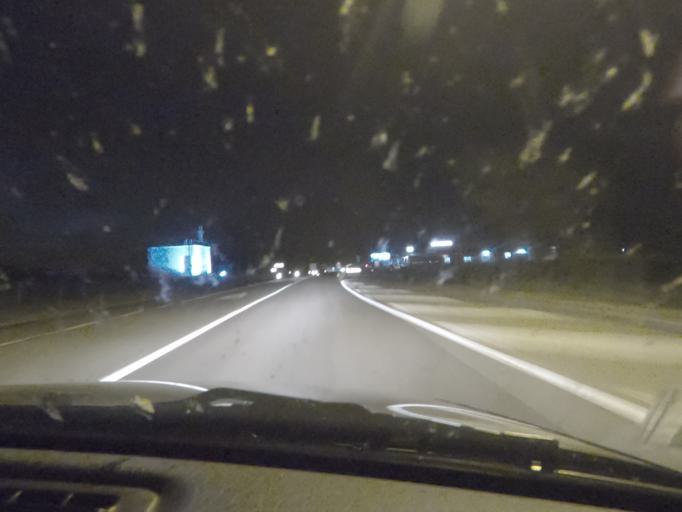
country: ES
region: Extremadura
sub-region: Provincia de Caceres
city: Moraleja
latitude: 40.0593
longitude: -6.6475
